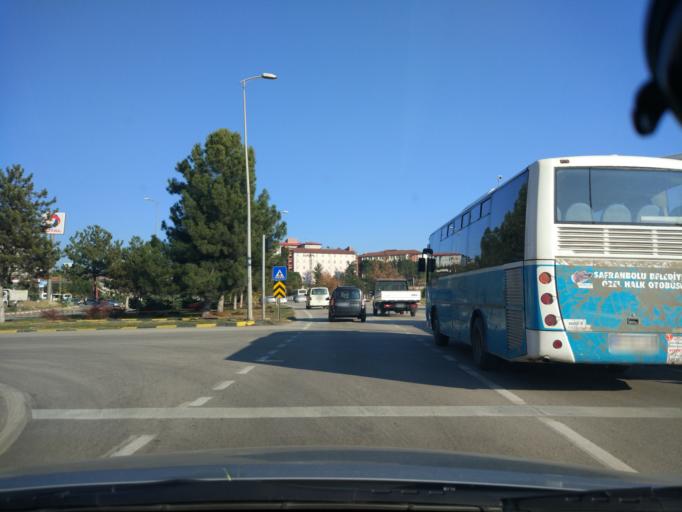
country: TR
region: Karabuk
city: Karabuk
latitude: 41.2188
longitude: 32.6529
